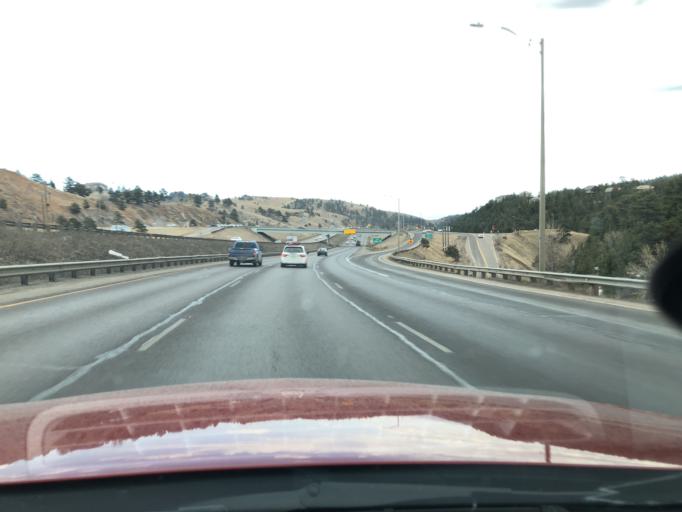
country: US
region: Colorado
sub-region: Jefferson County
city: Genesee
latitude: 39.7044
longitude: -105.2546
